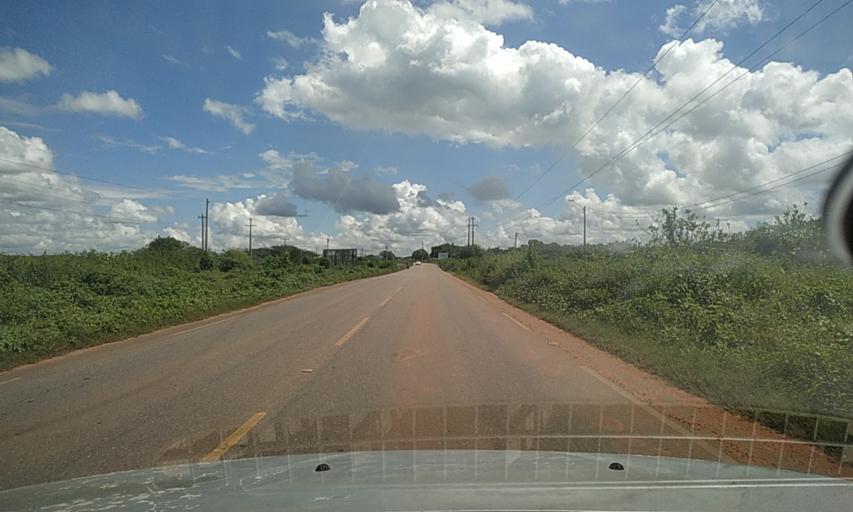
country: BR
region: Rio Grande do Norte
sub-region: Mossoro
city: Mossoro
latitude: -5.1862
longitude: -37.3839
